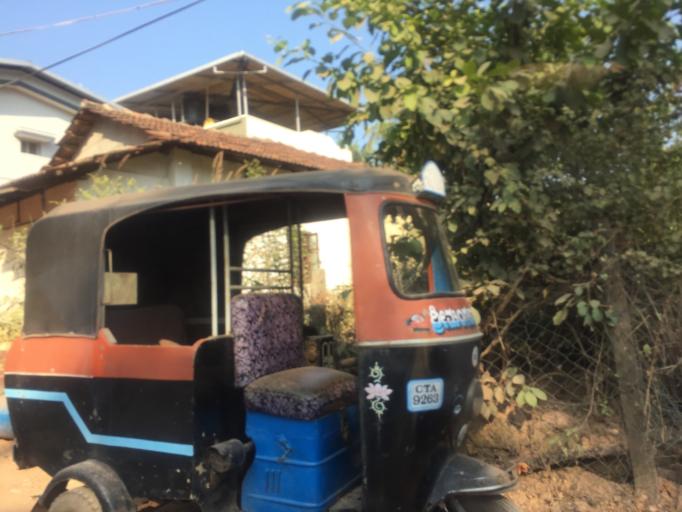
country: IN
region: Karnataka
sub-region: Dakshina Kannada
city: Ullal
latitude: 12.8442
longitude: 74.8471
